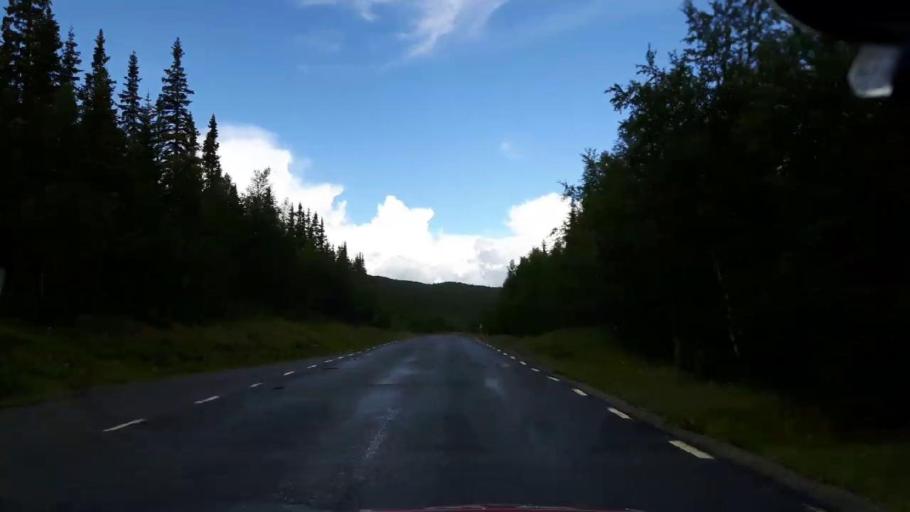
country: SE
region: Vaesterbotten
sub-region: Vilhelmina Kommun
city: Sjoberg
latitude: 65.0087
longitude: 15.1821
